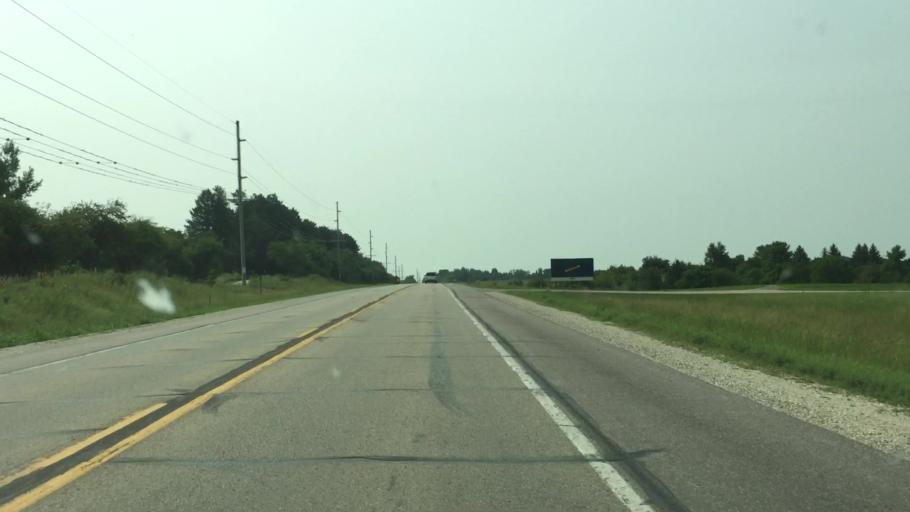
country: US
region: Iowa
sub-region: Dickinson County
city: Milford
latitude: 43.3520
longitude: -95.1799
